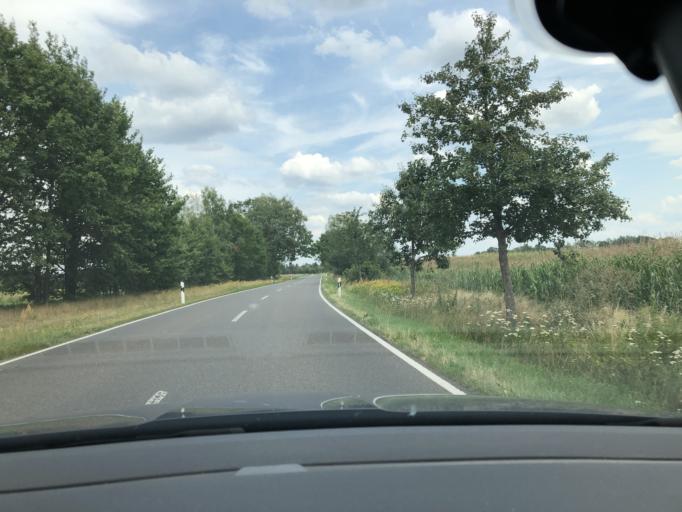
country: DE
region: Brandenburg
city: Schlepzig
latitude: 52.0744
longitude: 13.8662
